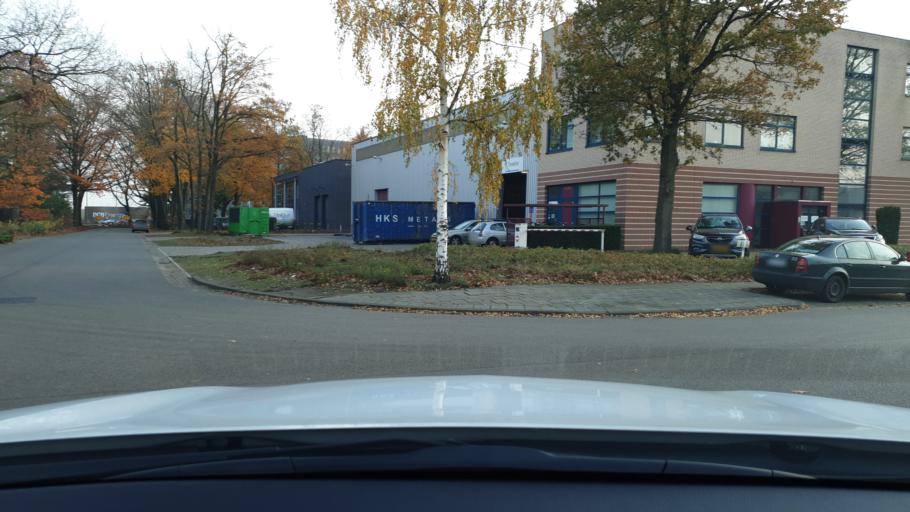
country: NL
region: North Brabant
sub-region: Gemeente Eindhoven
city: Meerhoven
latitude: 51.4578
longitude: 5.3991
